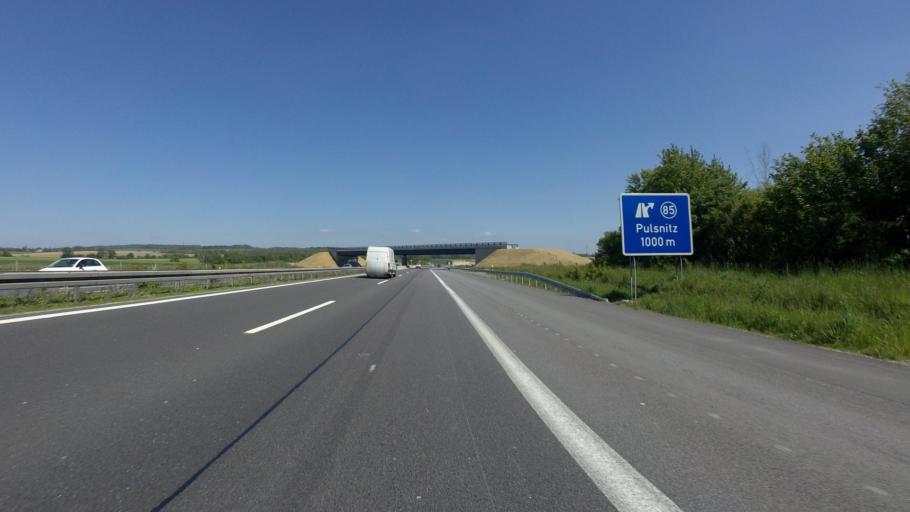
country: DE
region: Saxony
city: Lichtenberg
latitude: 51.1605
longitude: 13.9588
